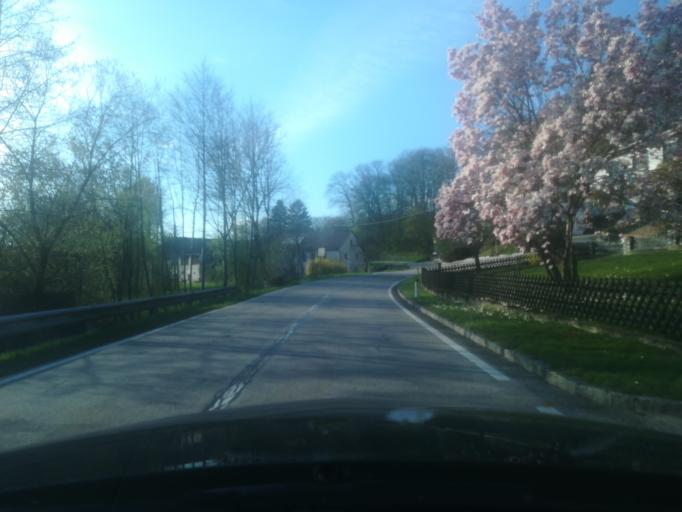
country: AT
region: Upper Austria
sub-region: Politischer Bezirk Perg
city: Bad Kreuzen
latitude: 48.2324
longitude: 14.8433
